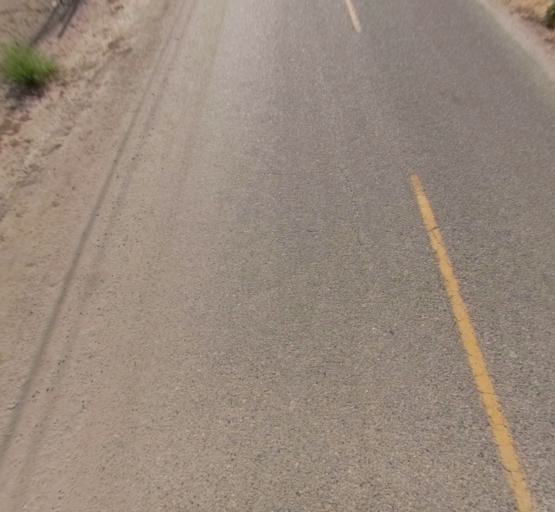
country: US
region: California
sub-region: Madera County
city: Madera
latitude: 36.9311
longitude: -120.1132
